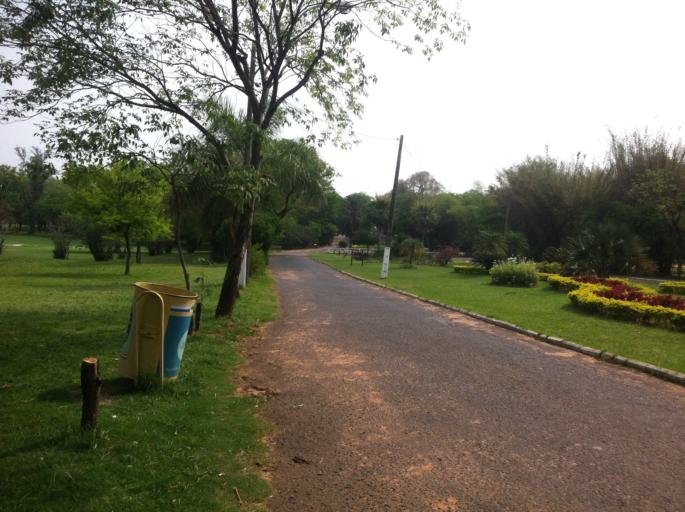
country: PY
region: Asuncion
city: Asuncion
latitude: -25.2503
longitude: -57.5759
